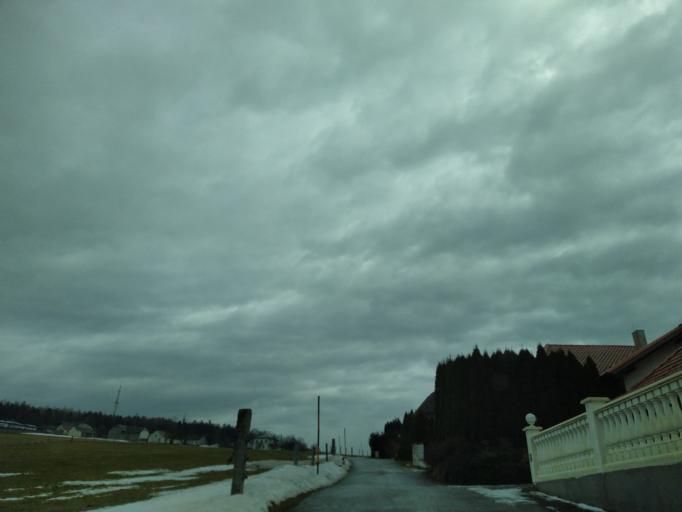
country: AT
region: Upper Austria
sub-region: Politischer Bezirk Urfahr-Umgebung
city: Kirchschlag bei Linz
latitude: 48.4133
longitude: 14.2643
